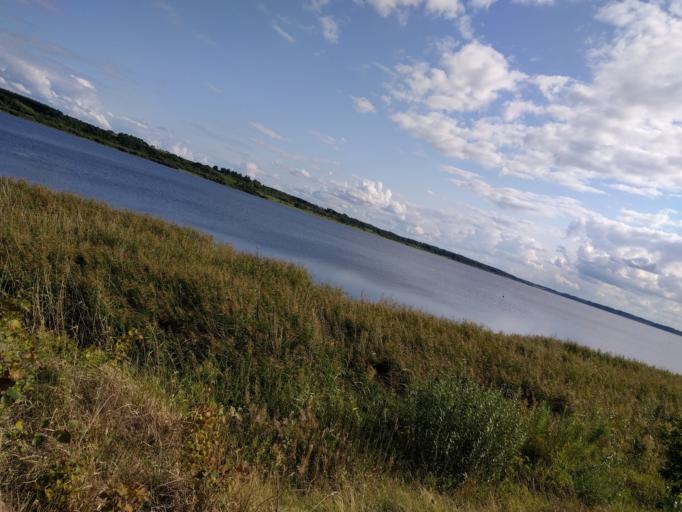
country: DK
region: Central Jutland
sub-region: Skive Kommune
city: Hojslev
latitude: 56.6012
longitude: 9.2860
